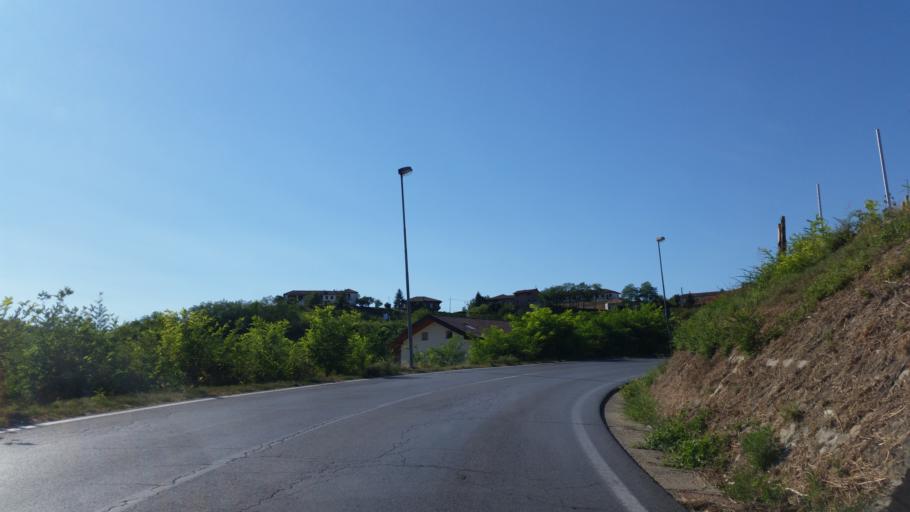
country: IT
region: Piedmont
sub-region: Provincia di Cuneo
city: Neive-Borgonovo
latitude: 44.7204
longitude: 8.1123
